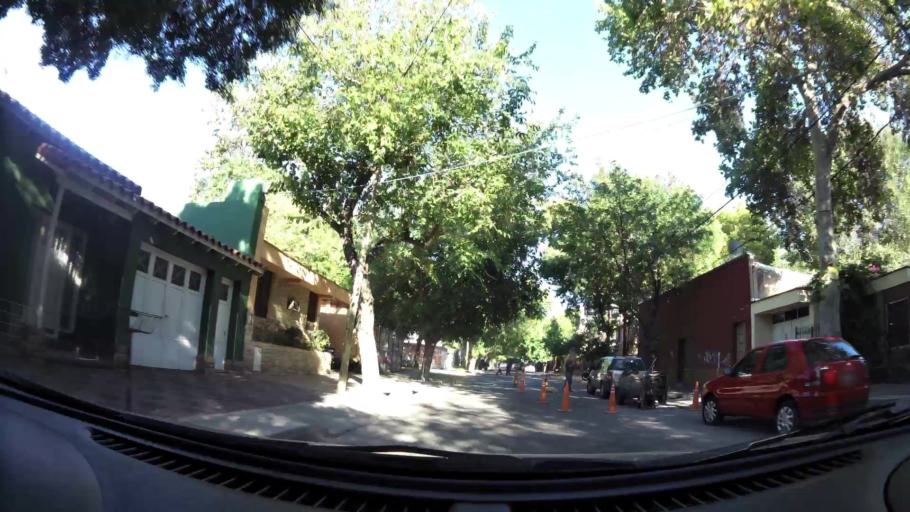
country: AR
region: Mendoza
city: Mendoza
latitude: -32.8738
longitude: -68.8334
